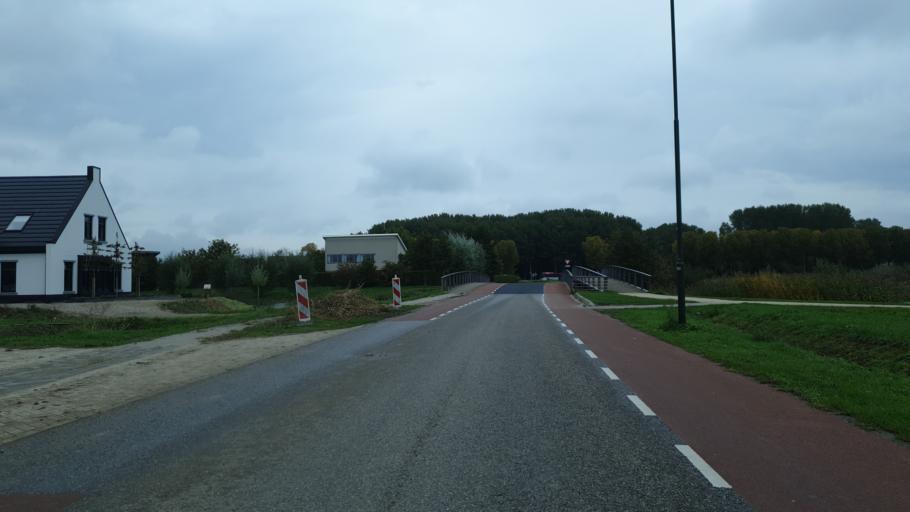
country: NL
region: Gelderland
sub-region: Gemeente Beuningen
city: Beuningen
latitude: 51.8510
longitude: 5.7781
